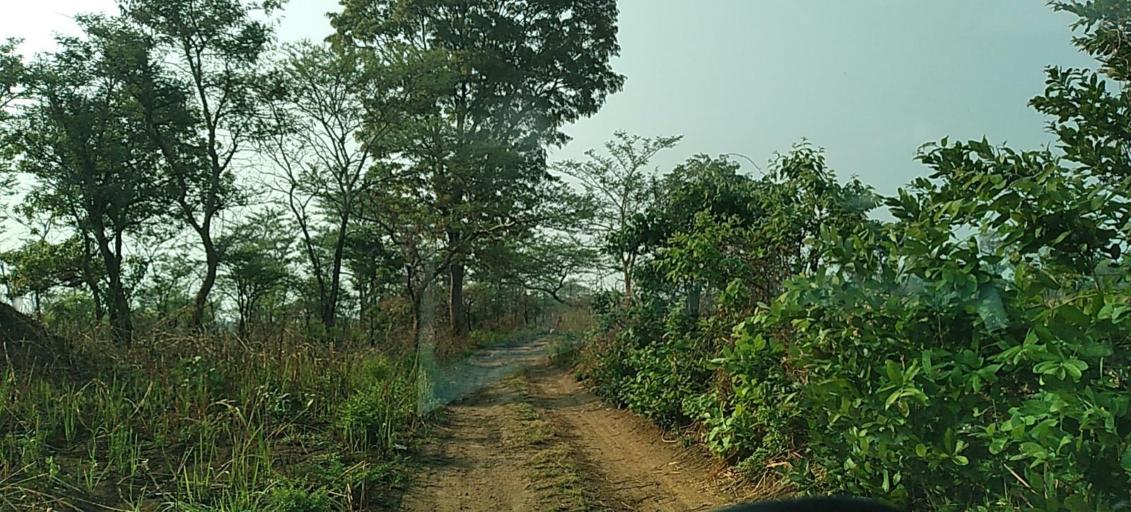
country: ZM
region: North-Western
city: Solwezi
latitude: -12.3774
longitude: 26.5633
